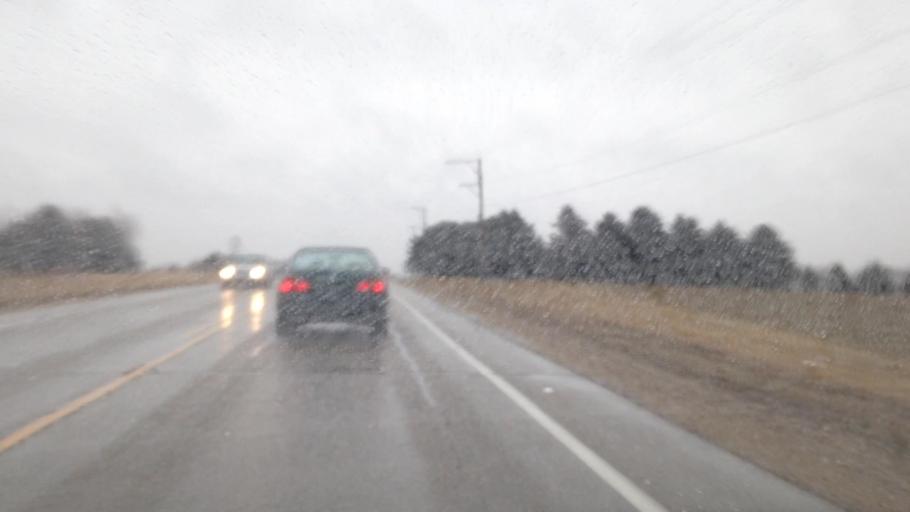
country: US
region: Wisconsin
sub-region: Washington County
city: Hartford
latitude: 43.4234
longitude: -88.3881
